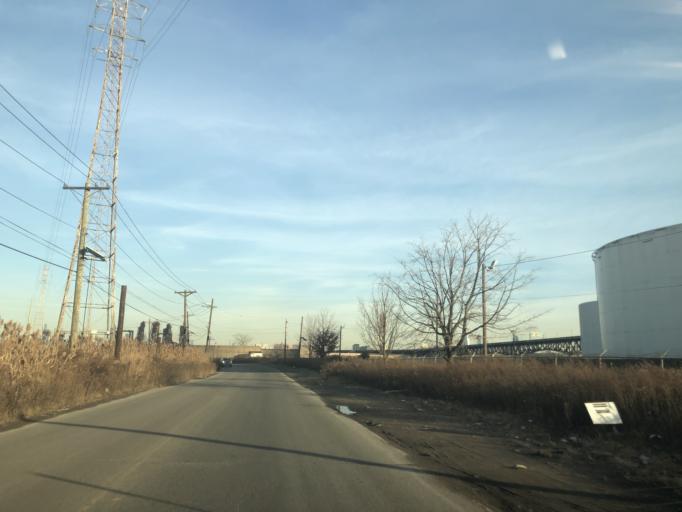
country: US
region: New Jersey
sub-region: Hudson County
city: Jersey City
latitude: 40.7389
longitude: -74.0957
